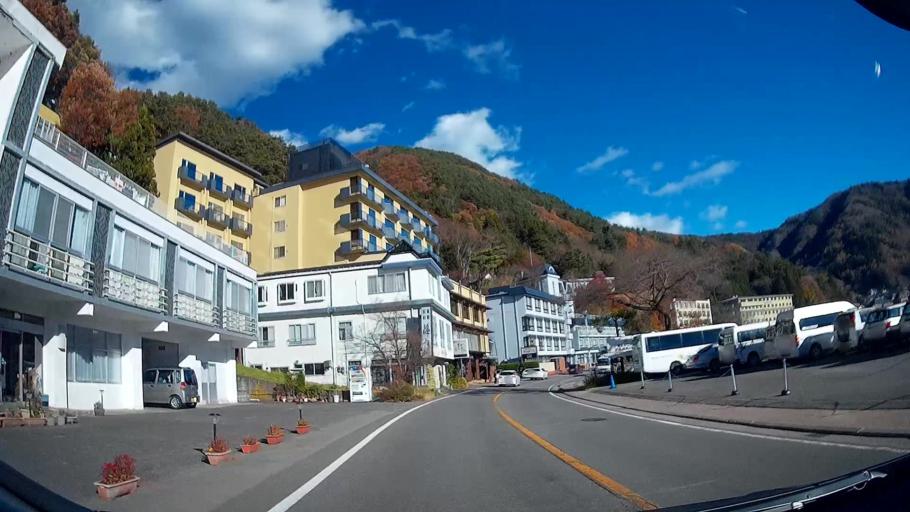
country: JP
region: Yamanashi
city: Fujikawaguchiko
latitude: 35.5133
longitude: 138.7721
